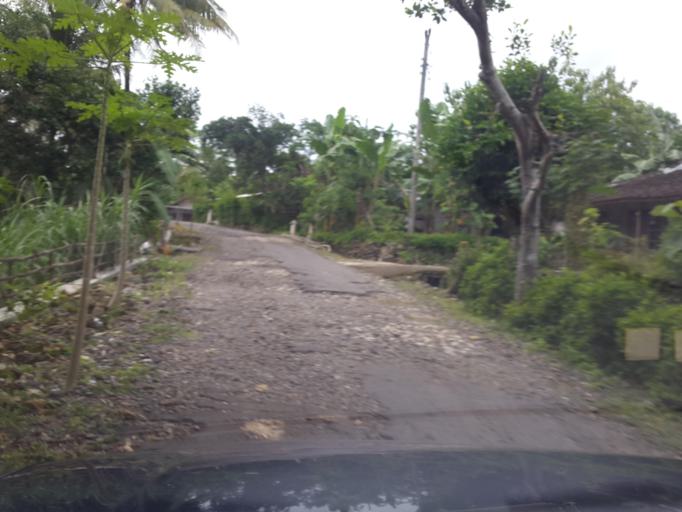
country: ID
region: Daerah Istimewa Yogyakarta
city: Wonosari
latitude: -7.8645
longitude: 110.6687
